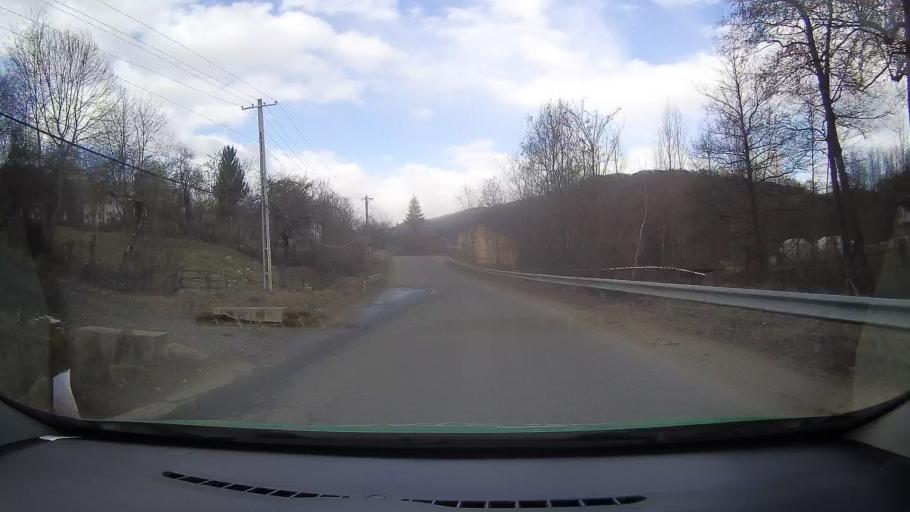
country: RO
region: Dambovita
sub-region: Comuna Visinesti
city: Visinesti
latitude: 45.0726
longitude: 25.5454
